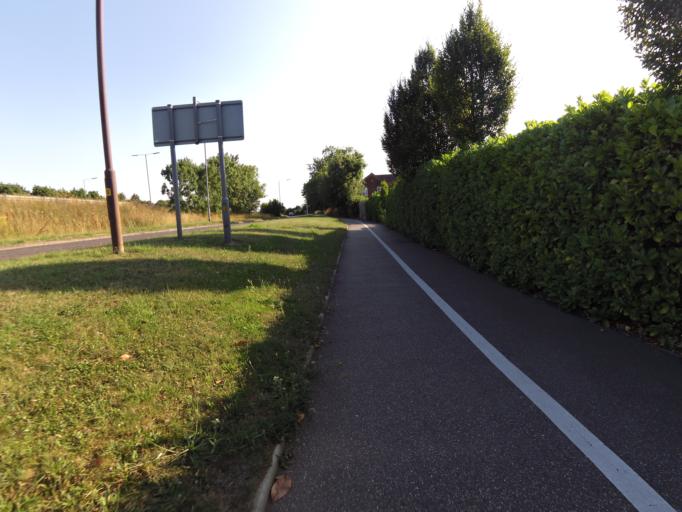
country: GB
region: England
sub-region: Essex
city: Chelmsford
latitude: 51.7445
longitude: 0.5001
